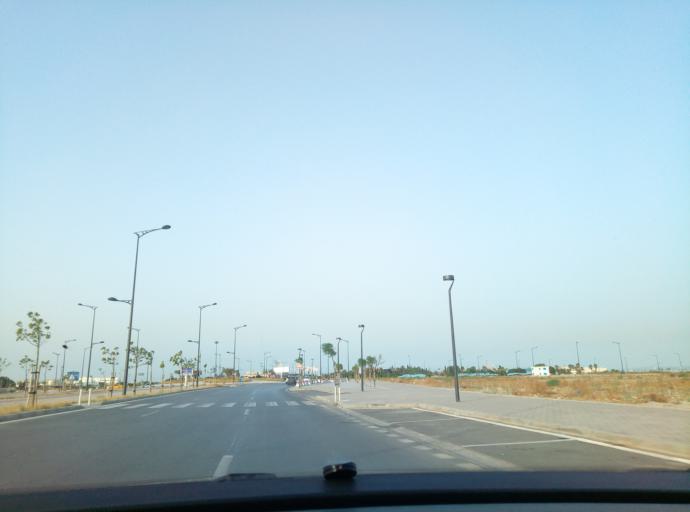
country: TN
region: Ariana
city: Ariana
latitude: 36.8288
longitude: 10.2118
